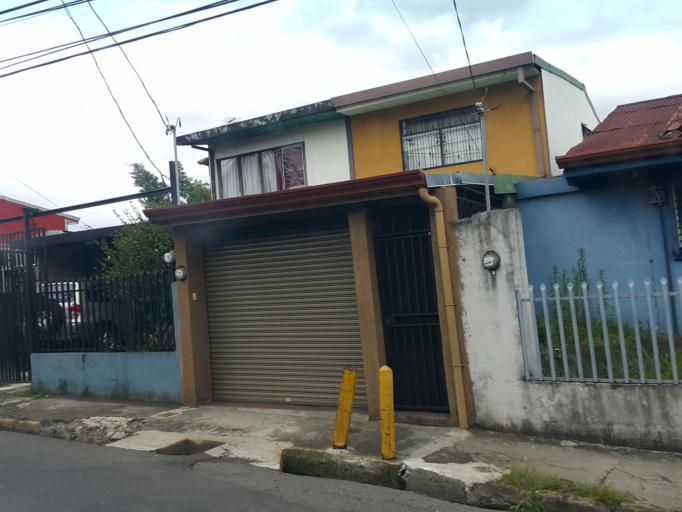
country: CR
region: Heredia
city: Mercedes
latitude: 10.0178
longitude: -84.1243
